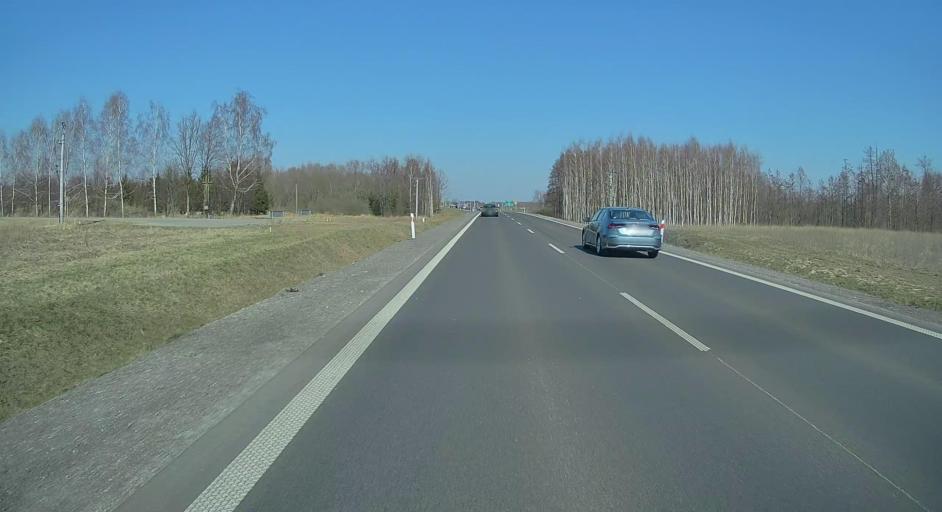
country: PL
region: Subcarpathian Voivodeship
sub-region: Powiat nizanski
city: Raclawice
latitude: 50.5138
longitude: 22.1723
